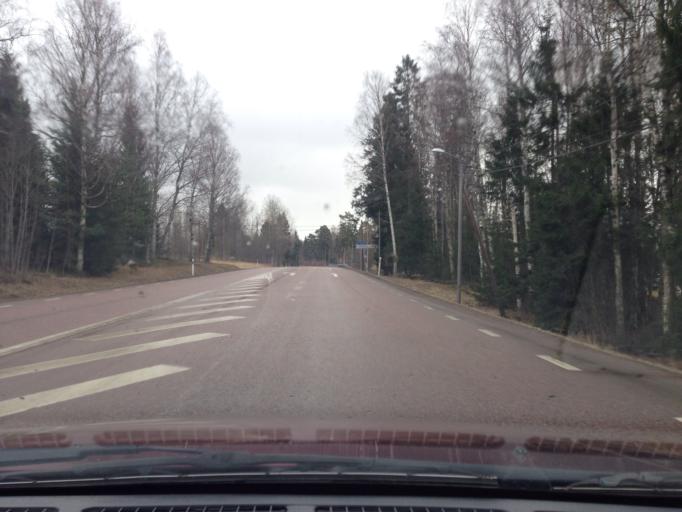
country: SE
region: Dalarna
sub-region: Ludvika Kommun
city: Ludvika
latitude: 60.1534
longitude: 15.2584
